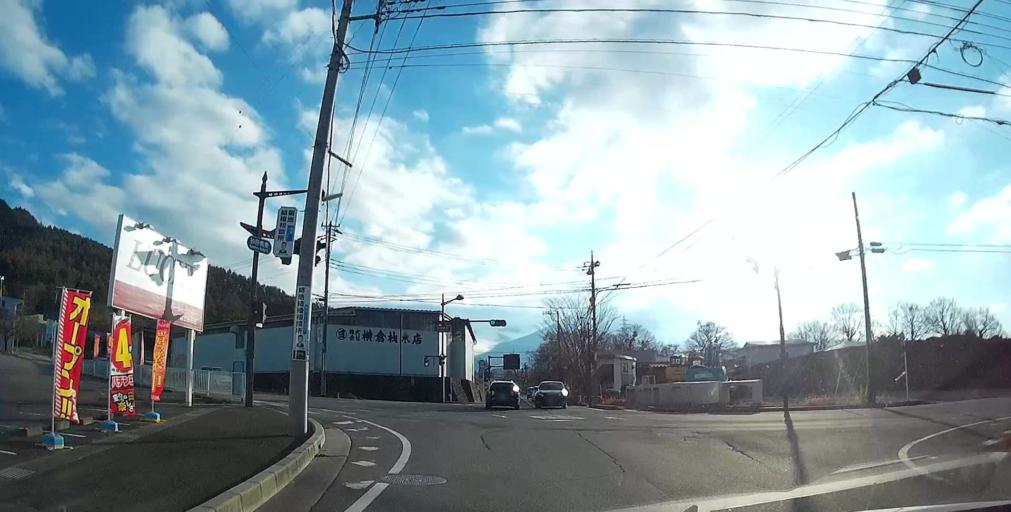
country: JP
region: Yamanashi
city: Fujikawaguchiko
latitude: 35.4779
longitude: 138.8161
